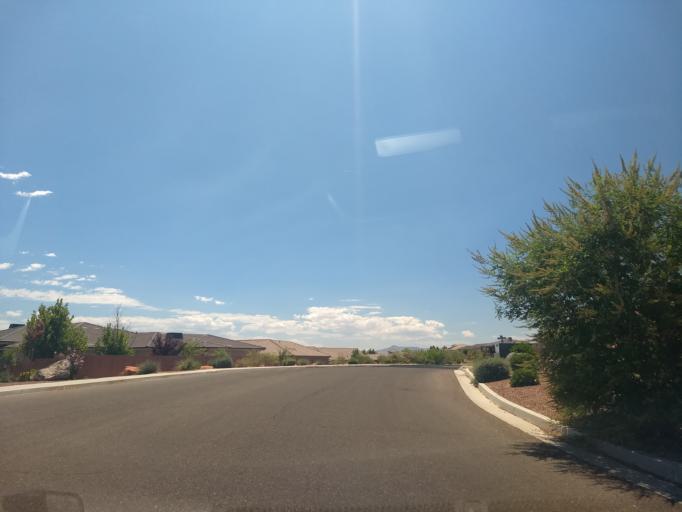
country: US
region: Utah
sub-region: Washington County
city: Washington
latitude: 37.1548
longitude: -113.5310
